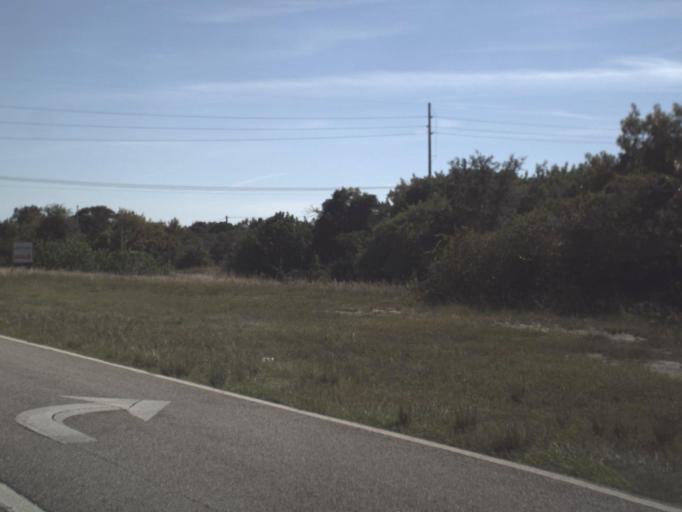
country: US
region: Florida
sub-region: Highlands County
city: Lake Placid
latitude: 27.2762
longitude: -81.3528
